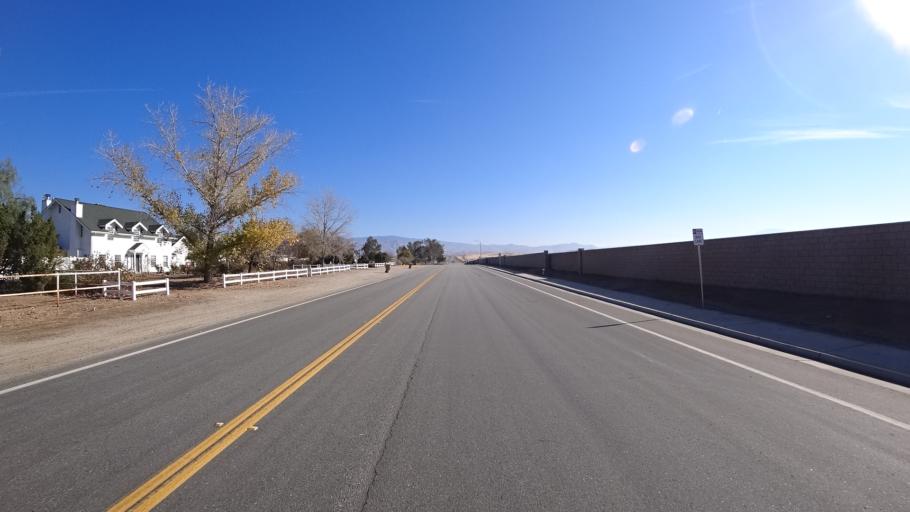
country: US
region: California
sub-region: Kern County
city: Oildale
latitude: 35.4125
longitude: -118.8842
